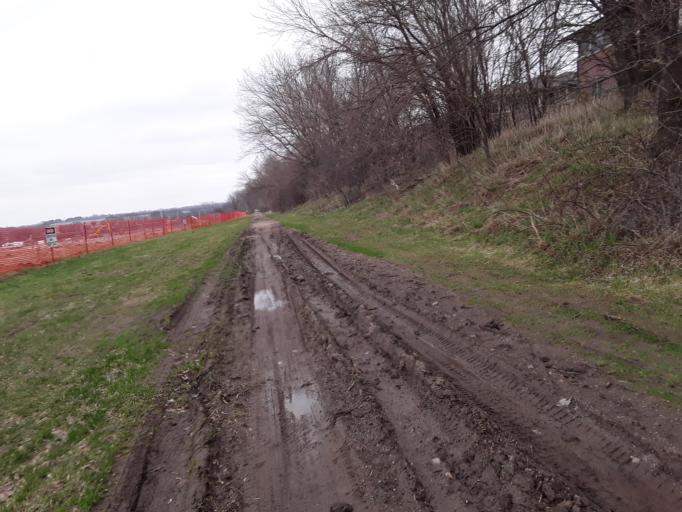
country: US
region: Nebraska
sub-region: Lancaster County
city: Lincoln
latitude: 40.8513
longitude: -96.6015
